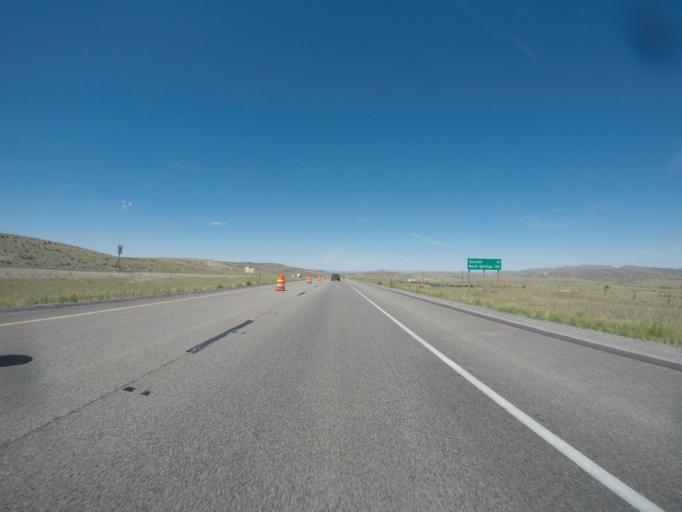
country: US
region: Wyoming
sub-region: Carbon County
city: Saratoga
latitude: 41.7422
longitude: -106.8510
